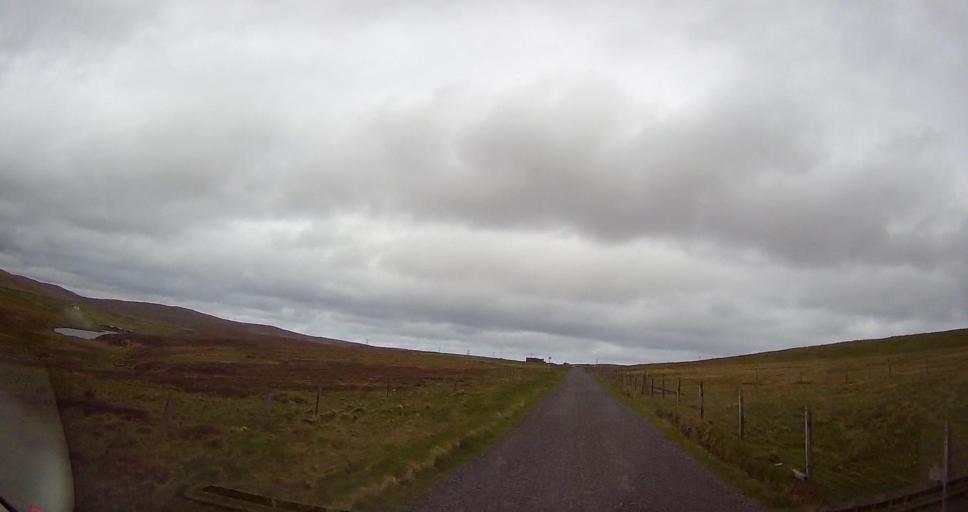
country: GB
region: Scotland
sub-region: Shetland Islands
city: Shetland
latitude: 60.7986
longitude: -0.8625
